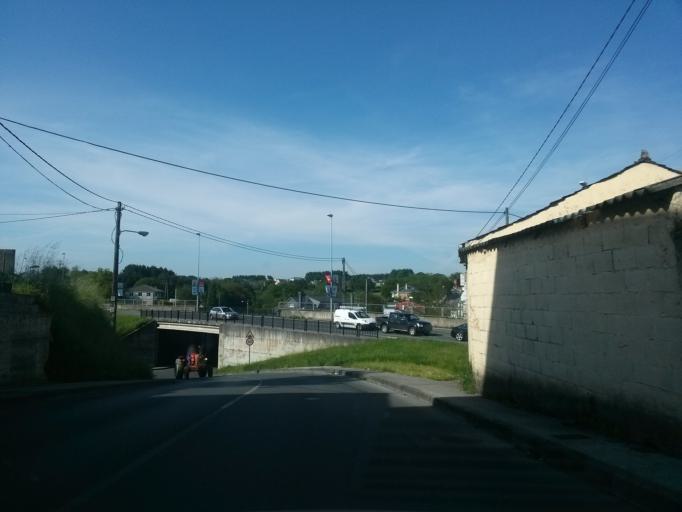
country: ES
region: Galicia
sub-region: Provincia de Lugo
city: Lugo
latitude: 43.0288
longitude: -7.5622
